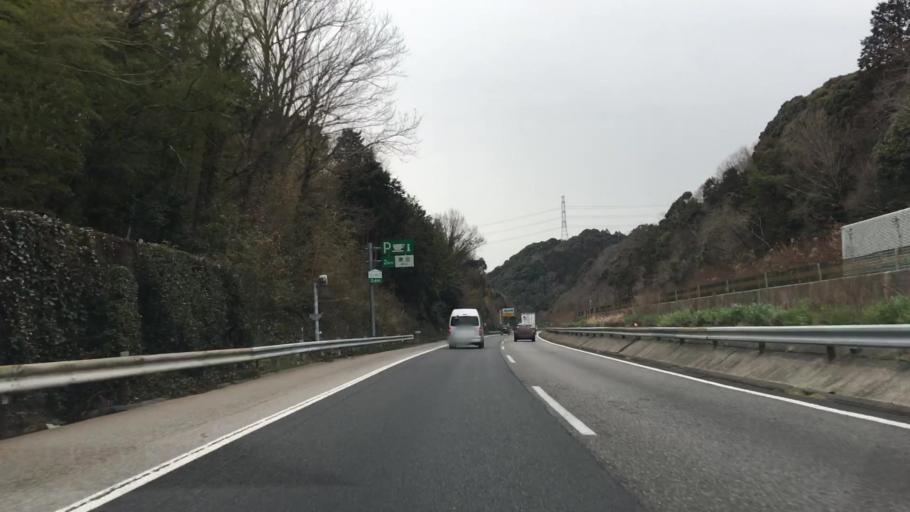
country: JP
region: Aichi
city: Gamagori
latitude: 34.9056
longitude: 137.2499
